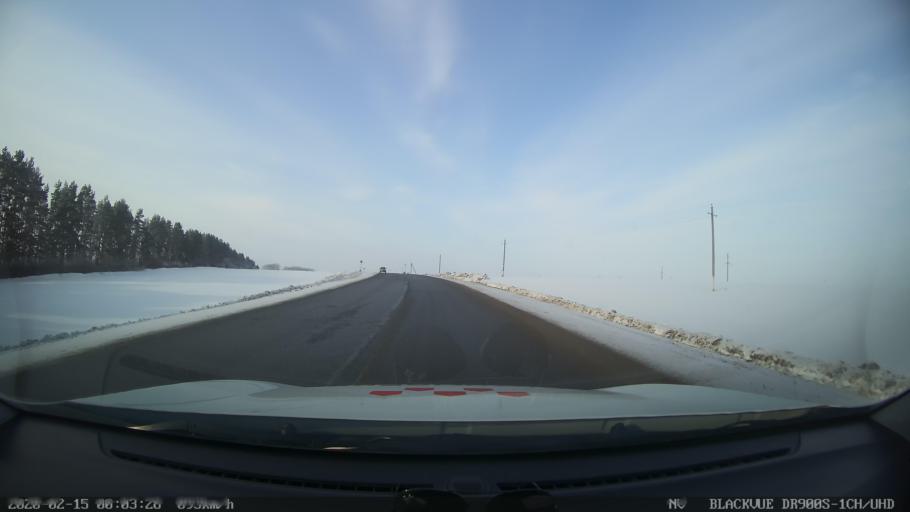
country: RU
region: Tatarstan
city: Kuybyshevskiy Zaton
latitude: 55.3723
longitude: 48.9974
